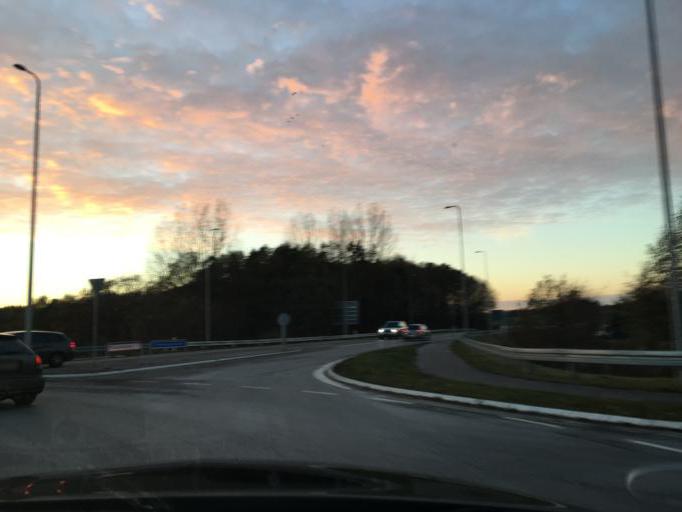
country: DK
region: Capital Region
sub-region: Fredensborg Kommune
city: Kokkedal
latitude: 55.9088
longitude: 12.4700
